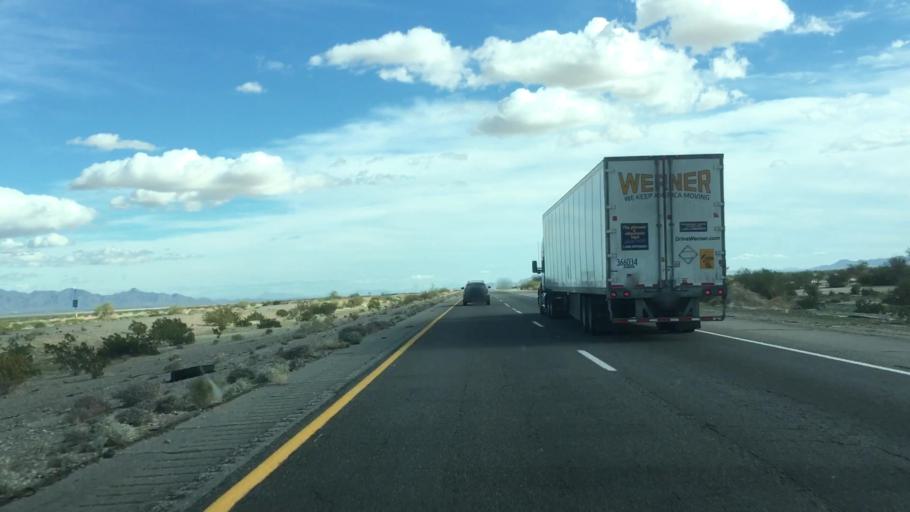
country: US
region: California
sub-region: Riverside County
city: Mesa Verde
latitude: 33.6459
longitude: -115.1203
